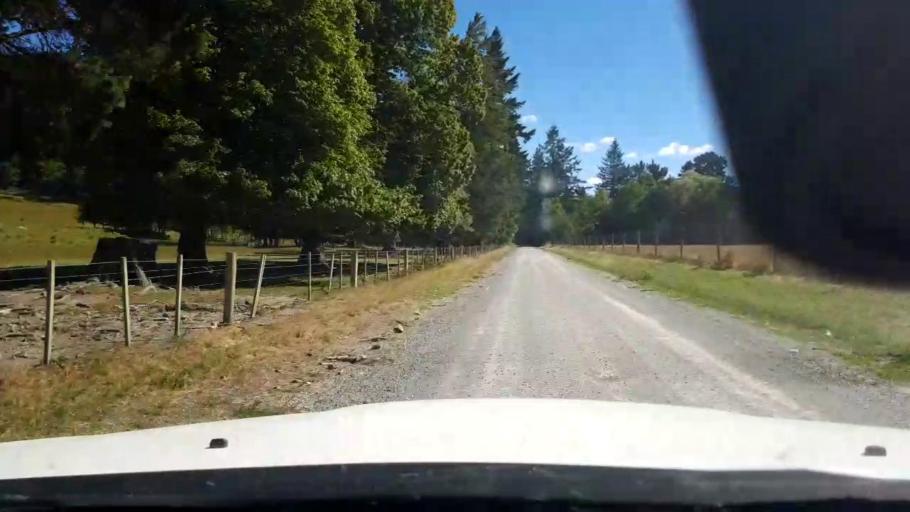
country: NZ
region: Canterbury
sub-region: Timaru District
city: Pleasant Point
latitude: -44.0274
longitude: 170.7436
